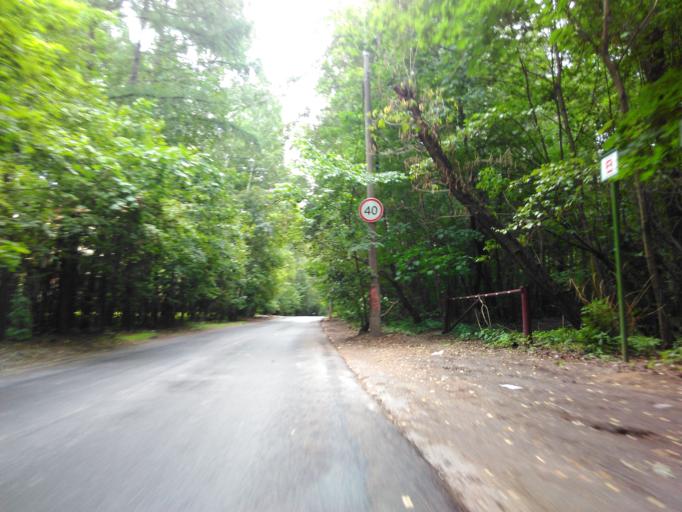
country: RU
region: Moscow
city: Rostokino
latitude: 55.8301
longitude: 37.6747
